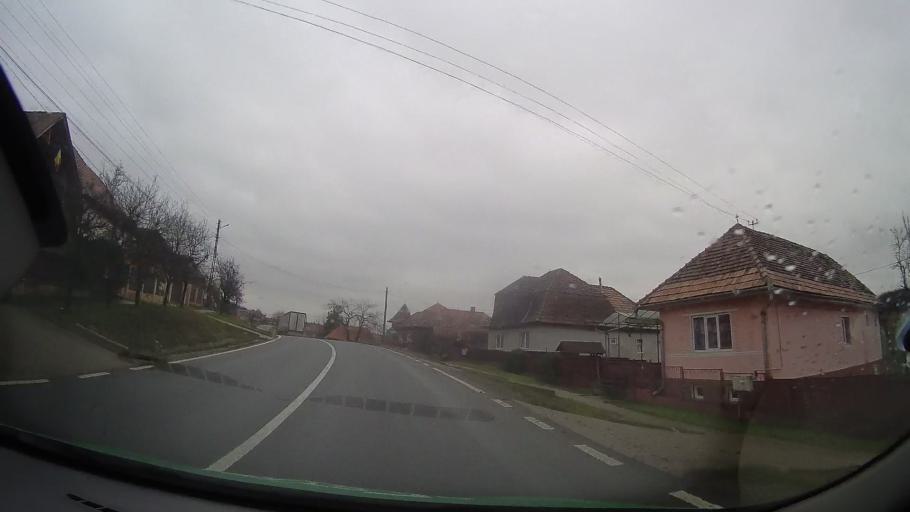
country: RO
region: Mures
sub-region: Comuna Lunca
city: Lunca
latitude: 46.8549
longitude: 24.5699
